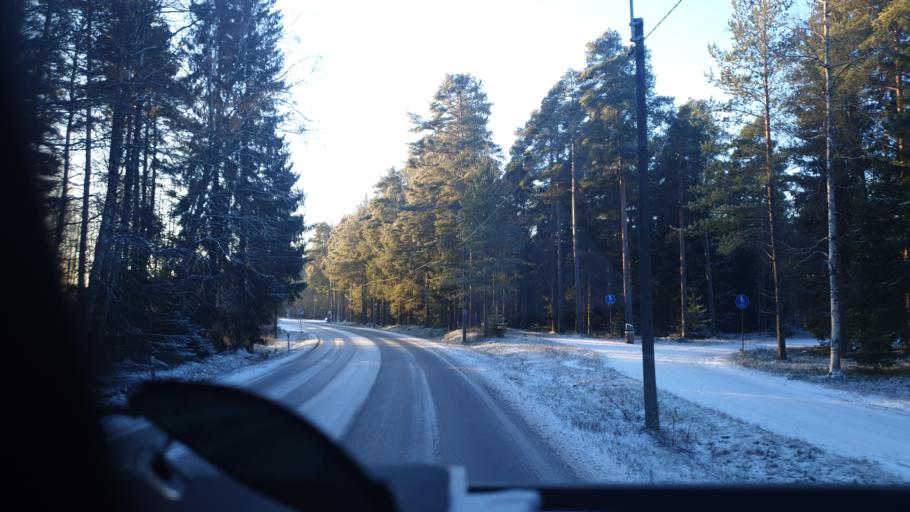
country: FI
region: Central Ostrobothnia
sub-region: Kokkola
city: Kokkola
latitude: 63.8264
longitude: 23.0947
